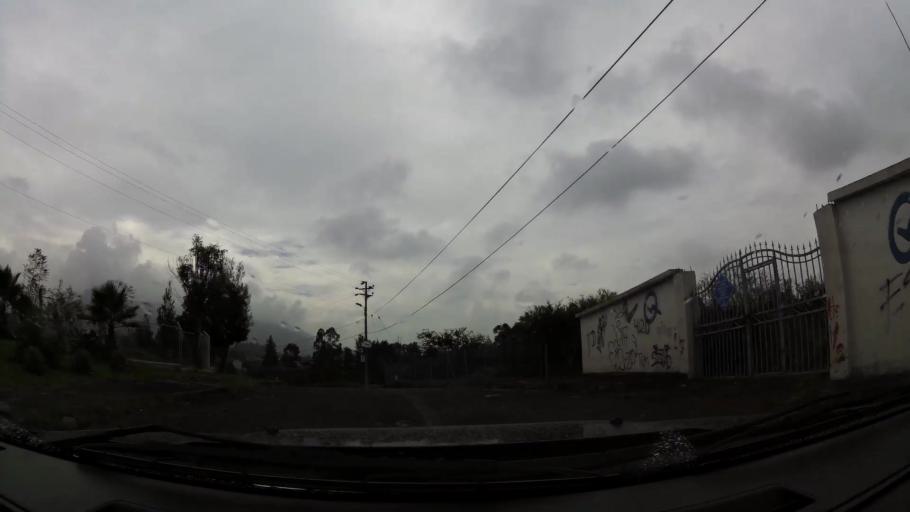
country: EC
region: Pichincha
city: Sangolqui
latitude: -0.2891
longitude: -78.4633
